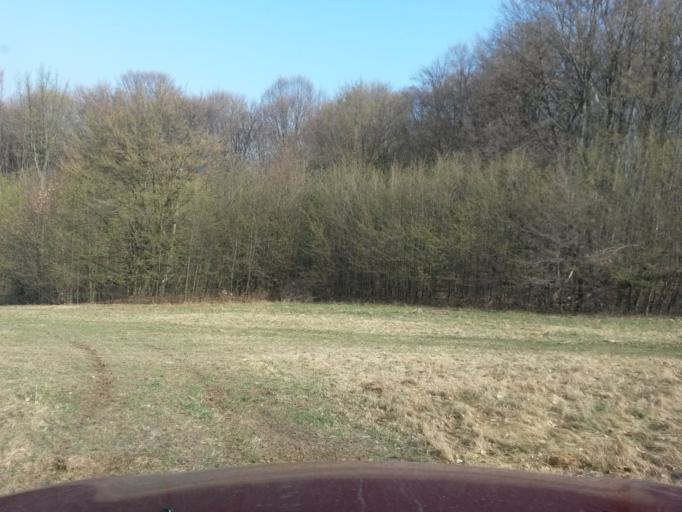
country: SK
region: Presovsky
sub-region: Okres Presov
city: Presov
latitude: 48.9289
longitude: 21.1482
